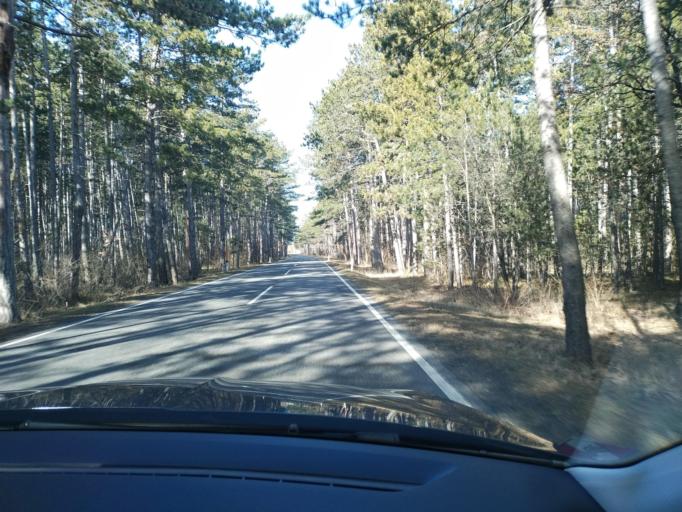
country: AT
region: Lower Austria
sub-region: Politischer Bezirk Neunkirchen
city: Breitenau
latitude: 47.7564
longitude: 16.1549
